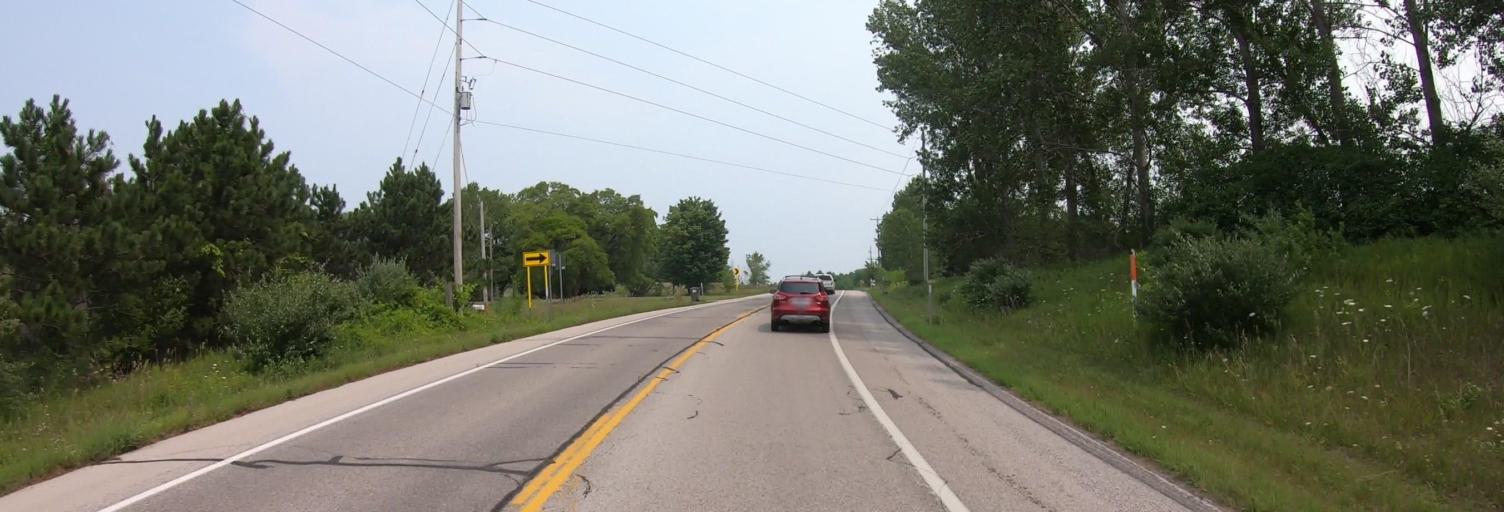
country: US
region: Michigan
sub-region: Leelanau County
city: Leland
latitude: 45.1074
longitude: -85.6406
